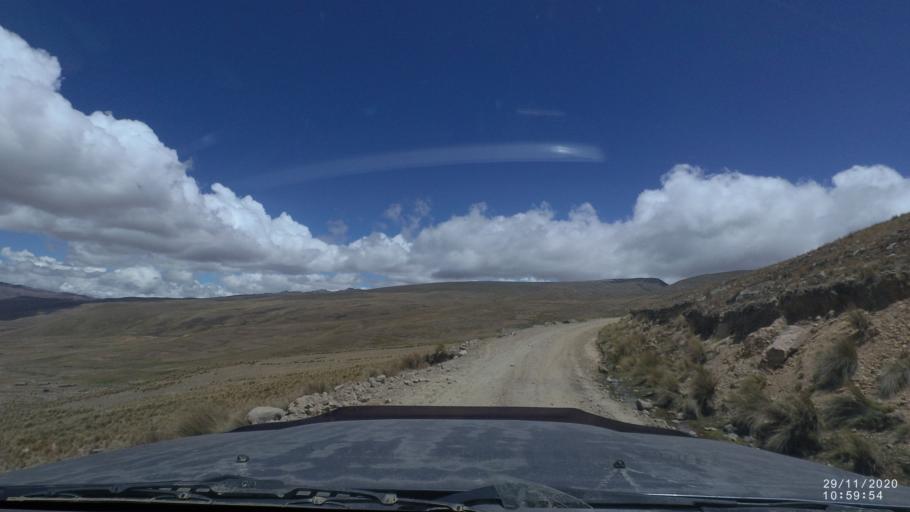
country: BO
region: Cochabamba
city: Cochabamba
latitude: -17.2064
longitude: -66.2287
